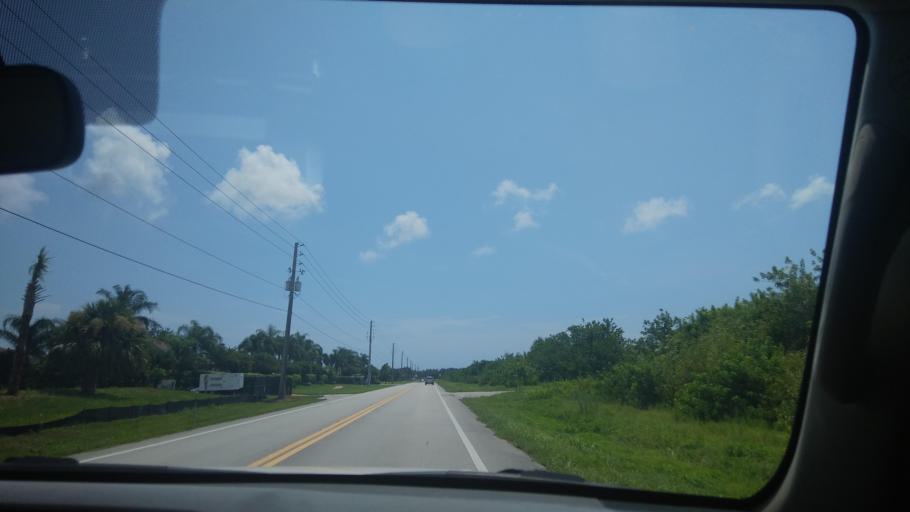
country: US
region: Florida
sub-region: Indian River County
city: Gifford
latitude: 27.6677
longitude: -80.4018
